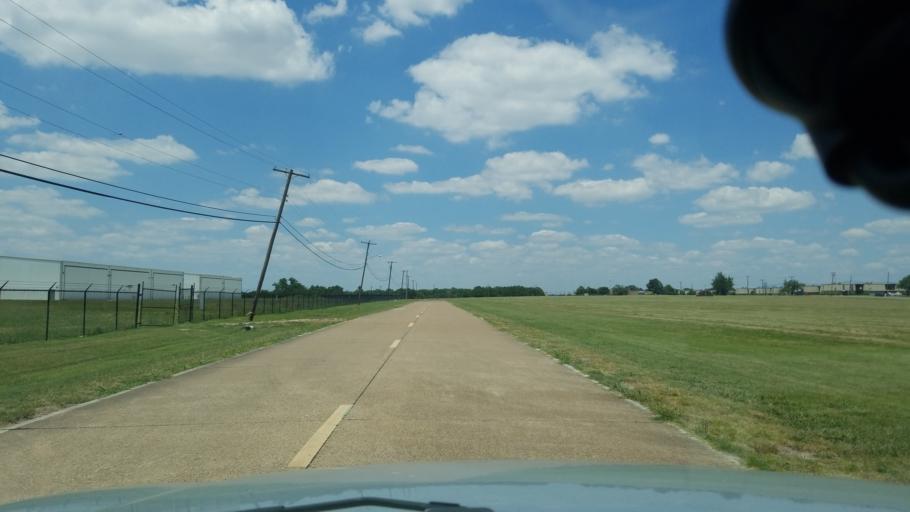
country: US
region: Texas
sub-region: Dallas County
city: Duncanville
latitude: 32.6800
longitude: -96.8590
